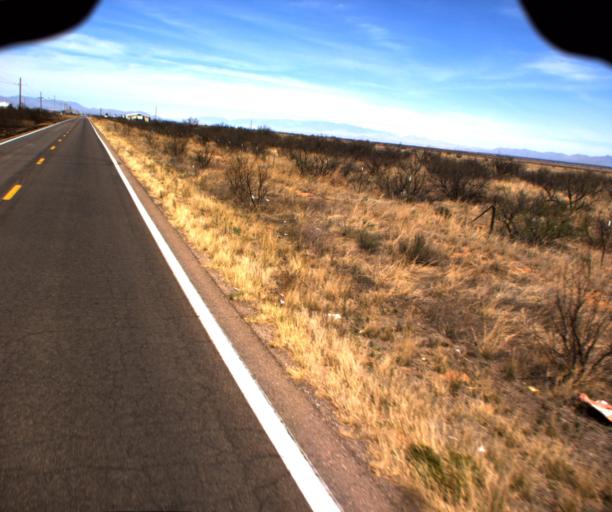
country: US
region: Arizona
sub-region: Cochise County
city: Willcox
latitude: 31.9811
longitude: -109.8514
